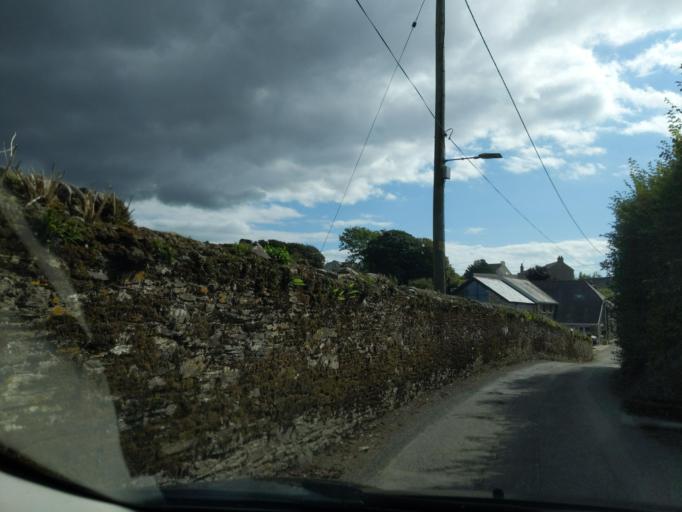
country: GB
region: England
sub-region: Plymouth
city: Plymstock
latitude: 50.3442
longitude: -4.0916
